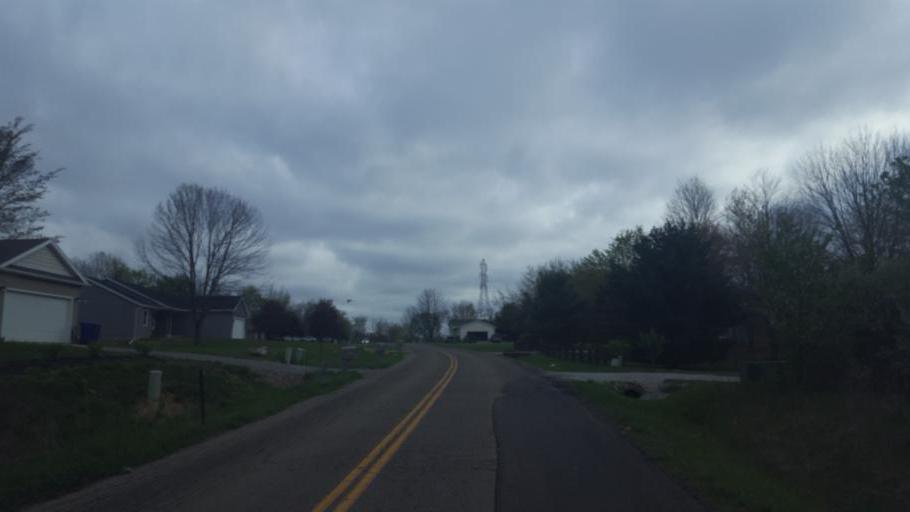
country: US
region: Ohio
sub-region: Knox County
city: Danville
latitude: 40.4576
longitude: -82.3494
